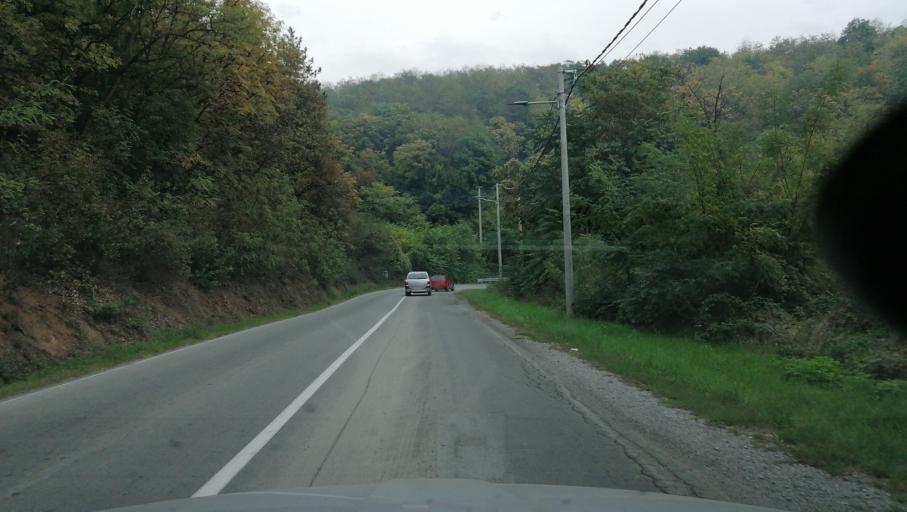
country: RS
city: Rusanj
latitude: 44.6860
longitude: 20.5042
